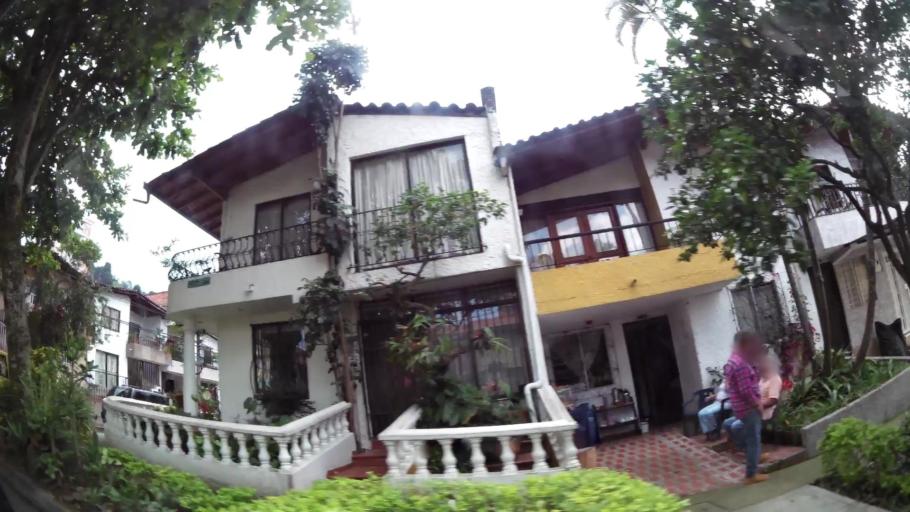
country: CO
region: Antioquia
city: Envigado
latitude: 6.1585
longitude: -75.5927
